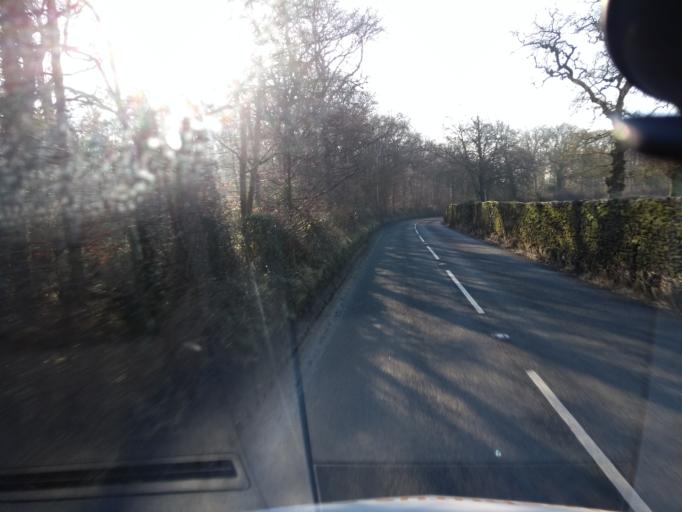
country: GB
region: England
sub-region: Somerset
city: Redlynch
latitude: 51.0951
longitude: -2.4196
